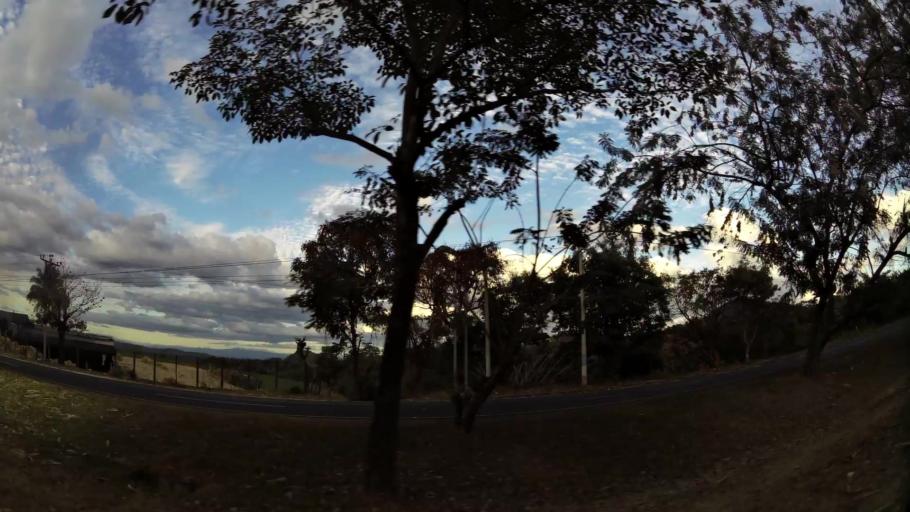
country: SV
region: San Vicente
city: San Vicente
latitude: 13.6725
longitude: -88.8427
